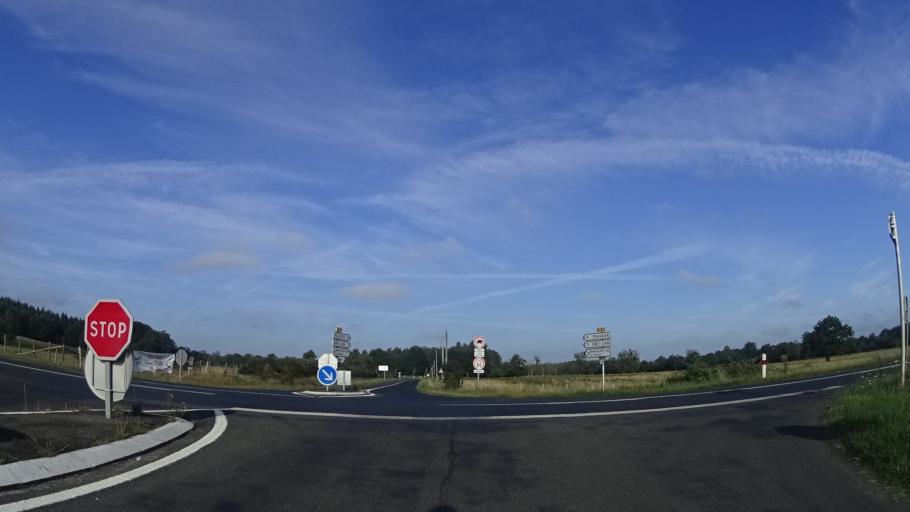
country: FR
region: Pays de la Loire
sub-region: Departement de la Sarthe
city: La Fleche
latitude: 47.6856
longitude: -0.0783
